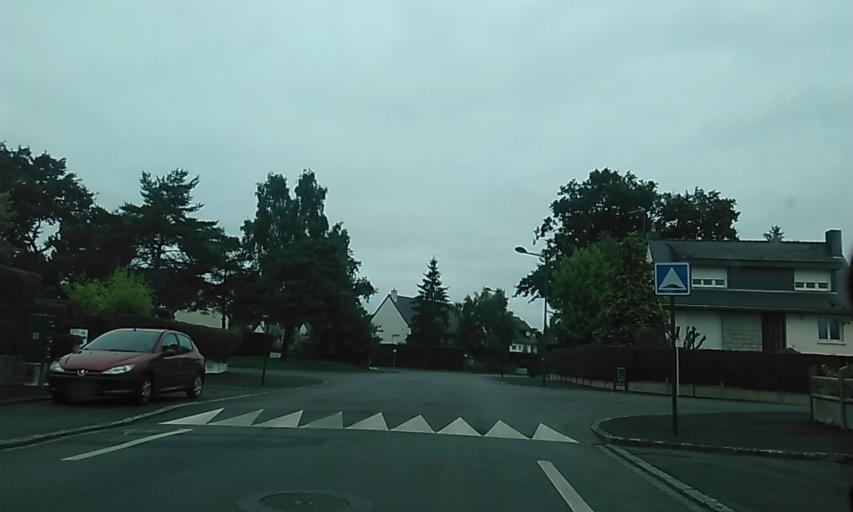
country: FR
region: Brittany
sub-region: Departement d'Ille-et-Vilaine
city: Chantepie
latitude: 48.0885
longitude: -1.6085
